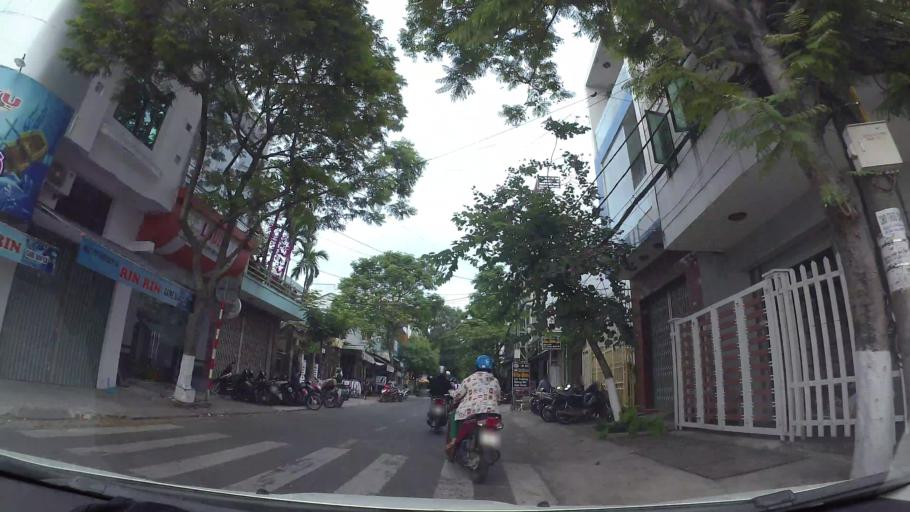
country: VN
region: Da Nang
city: Son Tra
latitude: 16.0550
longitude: 108.2366
